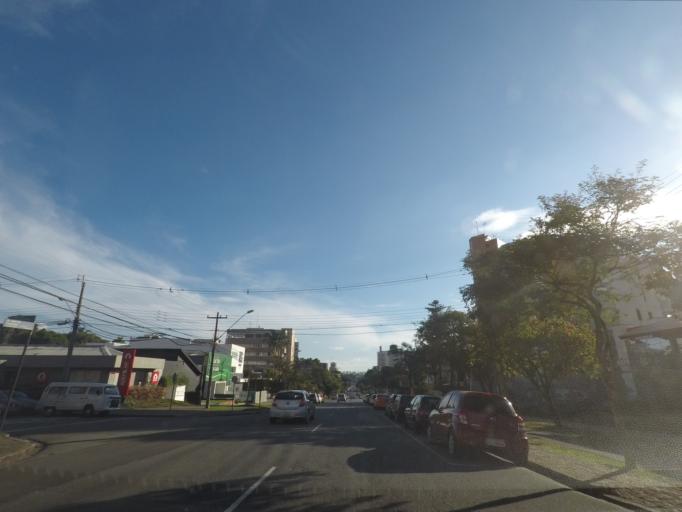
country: BR
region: Parana
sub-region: Curitiba
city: Curitiba
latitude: -25.4480
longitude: -49.2939
